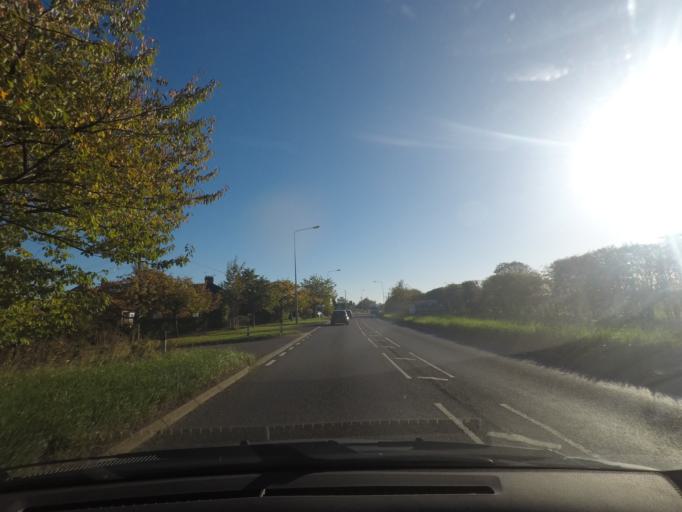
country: GB
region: England
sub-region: City of York
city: Holtby
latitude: 53.9554
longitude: -0.9788
